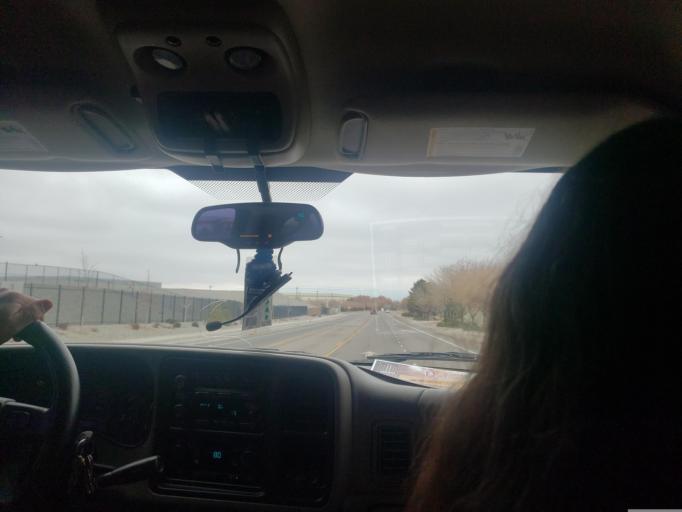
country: US
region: New Mexico
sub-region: Bernalillo County
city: Albuquerque
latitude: 35.0879
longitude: -106.7248
